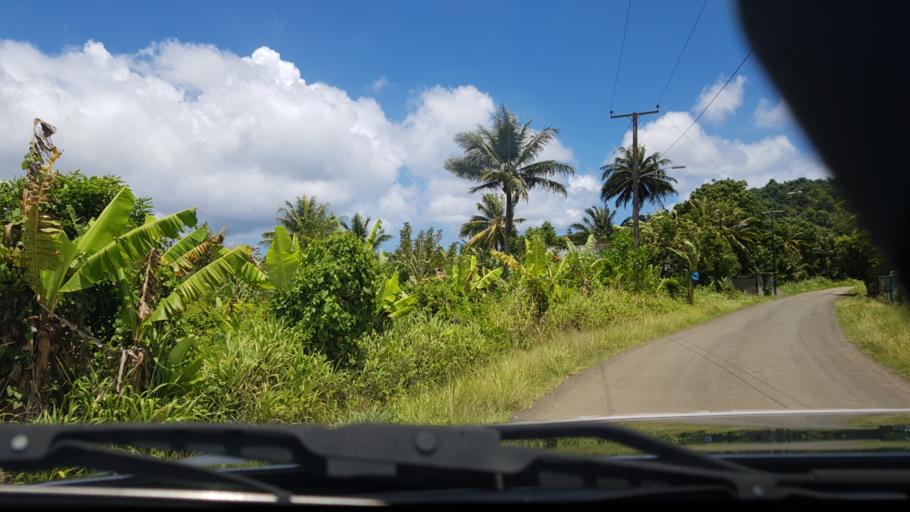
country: LC
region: Anse-la-Raye
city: Anse La Raye
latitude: 13.9493
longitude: -60.9946
